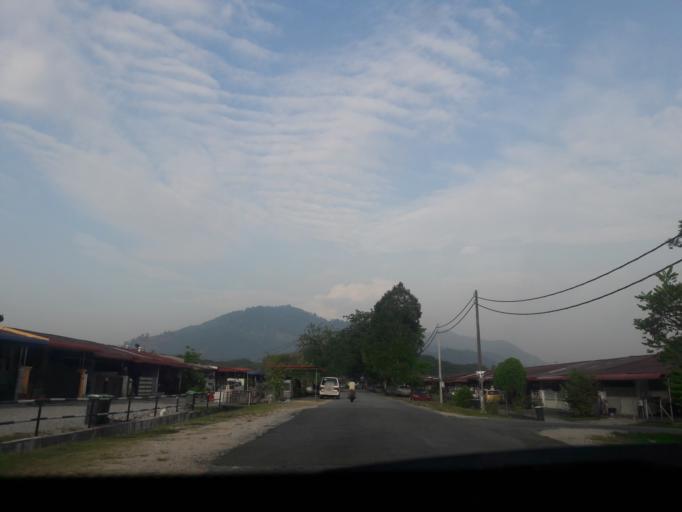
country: MY
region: Kedah
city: Kulim
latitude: 5.3792
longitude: 100.5316
